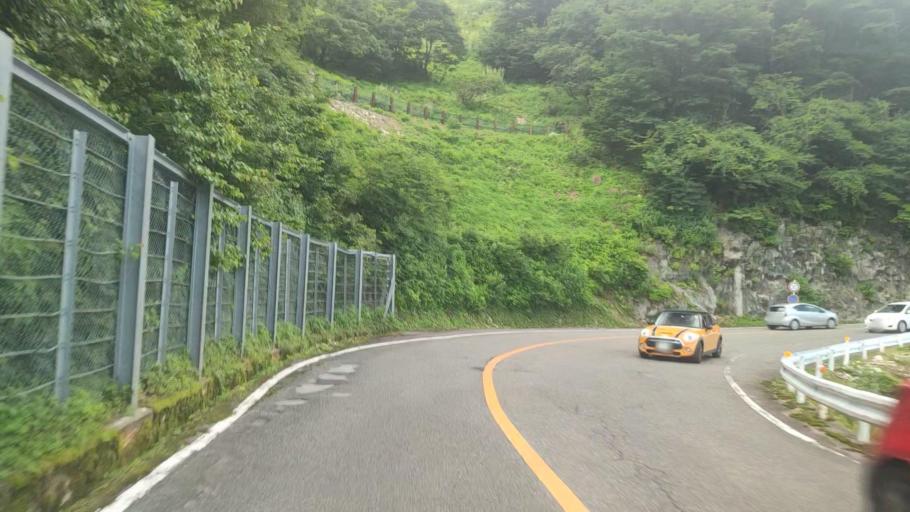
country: JP
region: Gifu
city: Tarui
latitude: 35.4179
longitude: 136.4183
